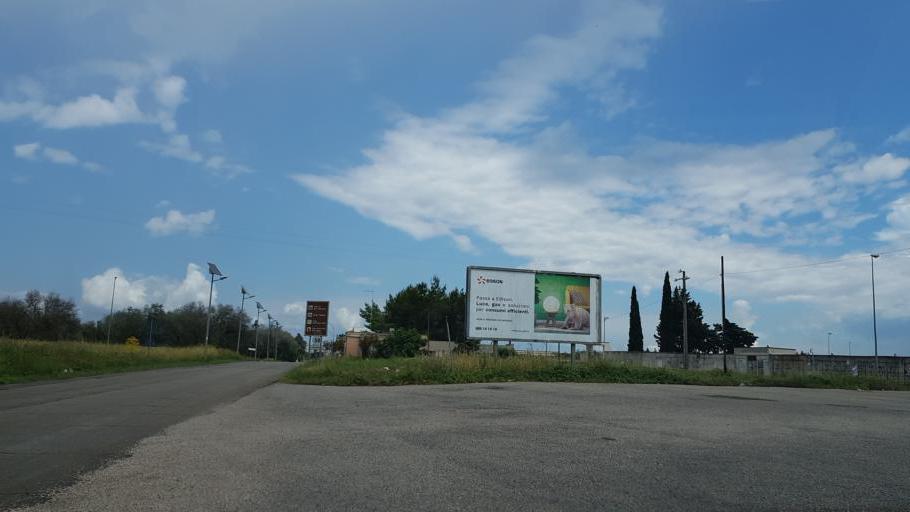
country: IT
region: Apulia
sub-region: Provincia di Brindisi
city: San Donaci
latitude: 40.4432
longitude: 17.9107
